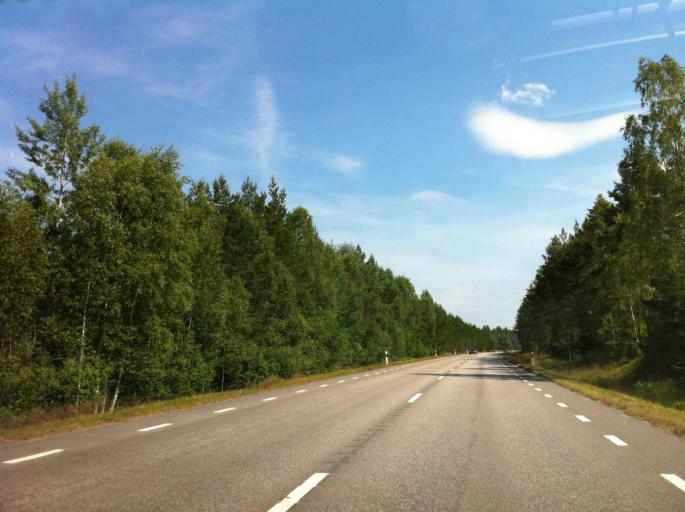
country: SE
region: Kalmar
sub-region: Nybro Kommun
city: Nybro
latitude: 56.8374
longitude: 15.7282
